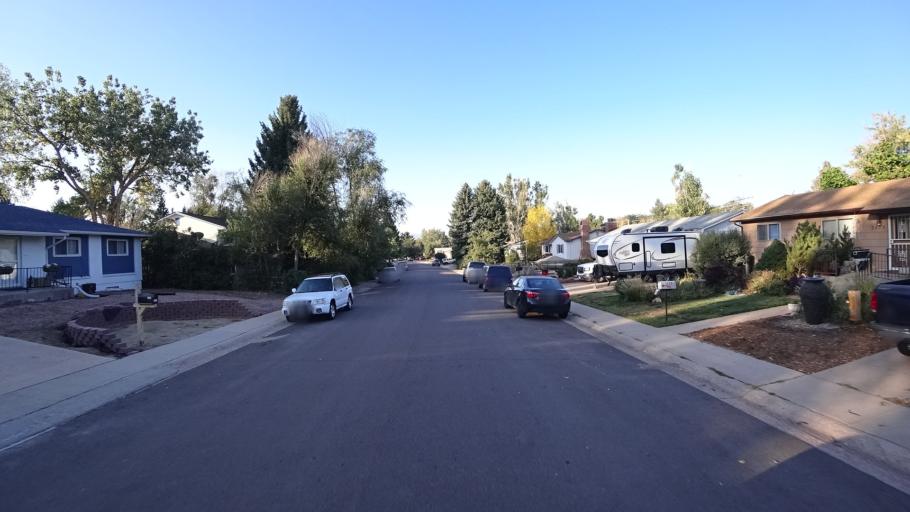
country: US
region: Colorado
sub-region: El Paso County
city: Cimarron Hills
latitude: 38.8941
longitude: -104.7645
